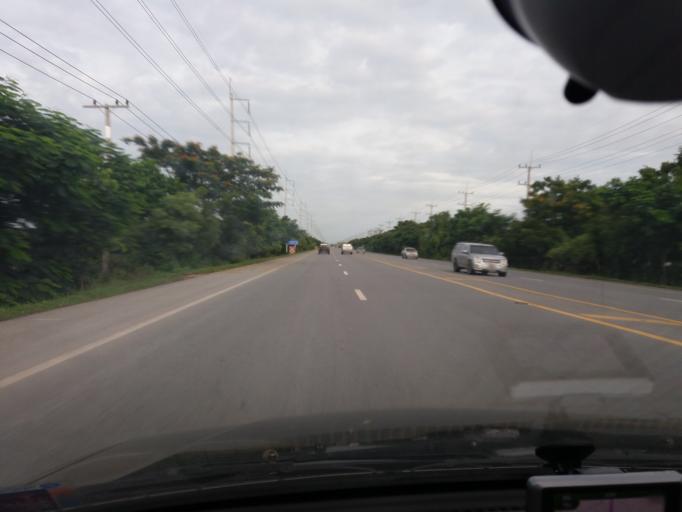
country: TH
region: Suphan Buri
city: U Thong
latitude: 14.3369
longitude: 99.8255
